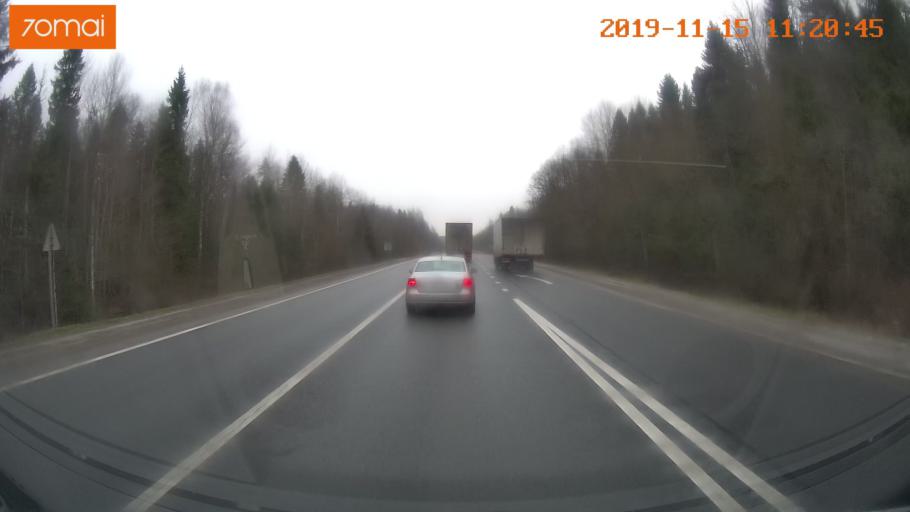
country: RU
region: Vologda
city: Molochnoye
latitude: 59.1425
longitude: 39.3224
